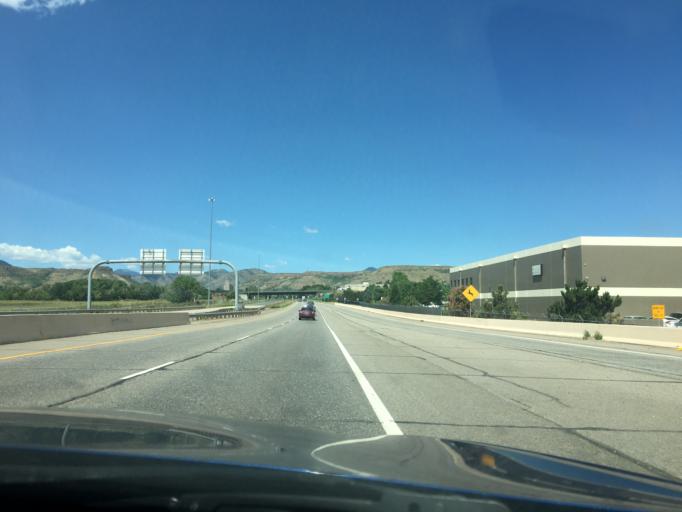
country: US
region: Colorado
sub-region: Jefferson County
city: Applewood
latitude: 39.7754
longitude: -105.1491
